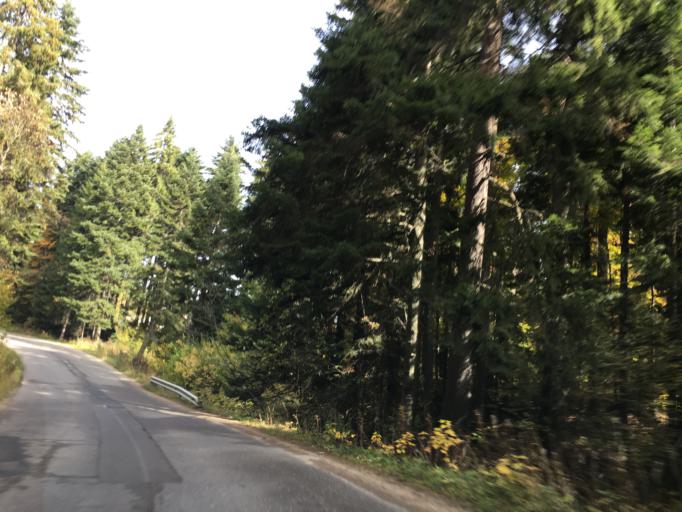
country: BG
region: Sofiya
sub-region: Obshtina Samokov
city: Samokov
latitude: 42.2699
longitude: 23.6140
